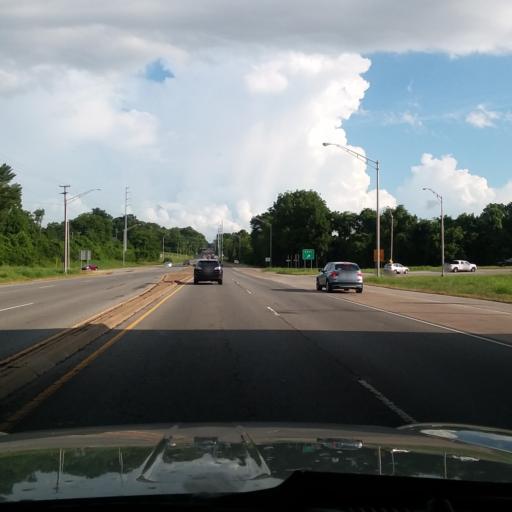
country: US
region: Tennessee
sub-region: Davidson County
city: Oak Hill
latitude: 36.1102
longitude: -86.7734
